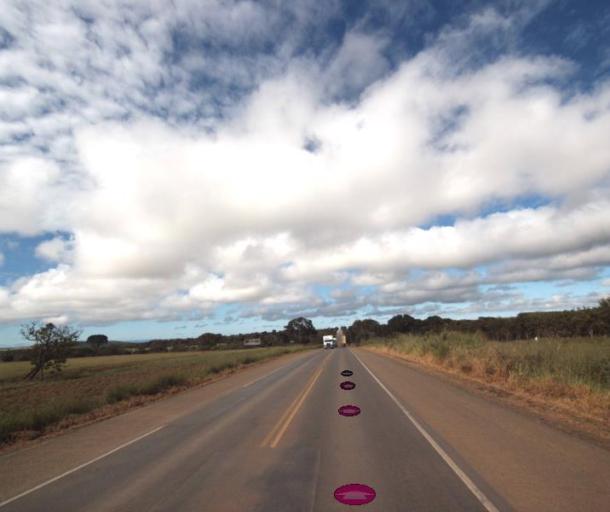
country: BR
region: Goias
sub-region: Uruacu
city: Uruacu
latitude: -14.7532
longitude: -49.2550
